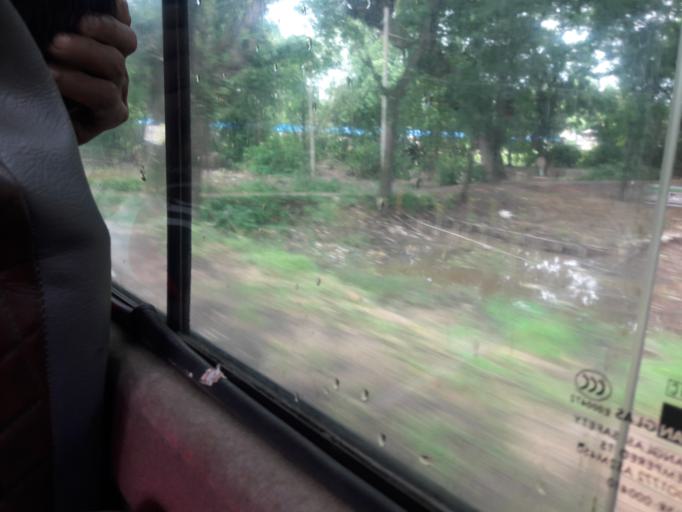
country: MM
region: Bago
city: Nyaunglebin
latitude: 17.7751
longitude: 96.6454
